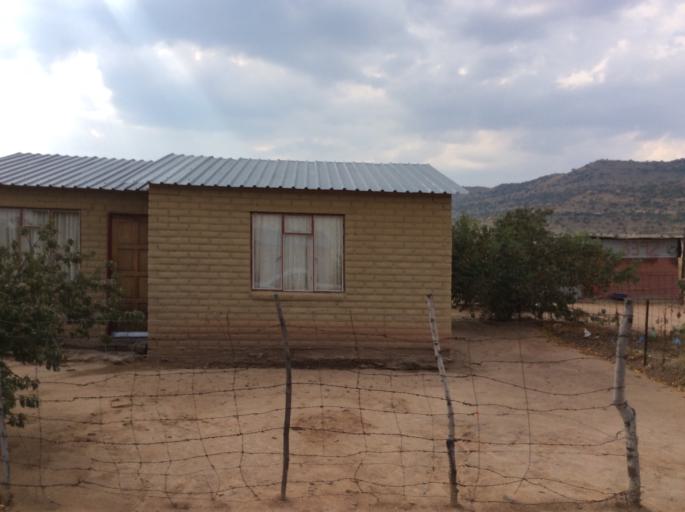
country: LS
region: Mafeteng
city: Mafeteng
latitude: -29.7094
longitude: 27.0122
